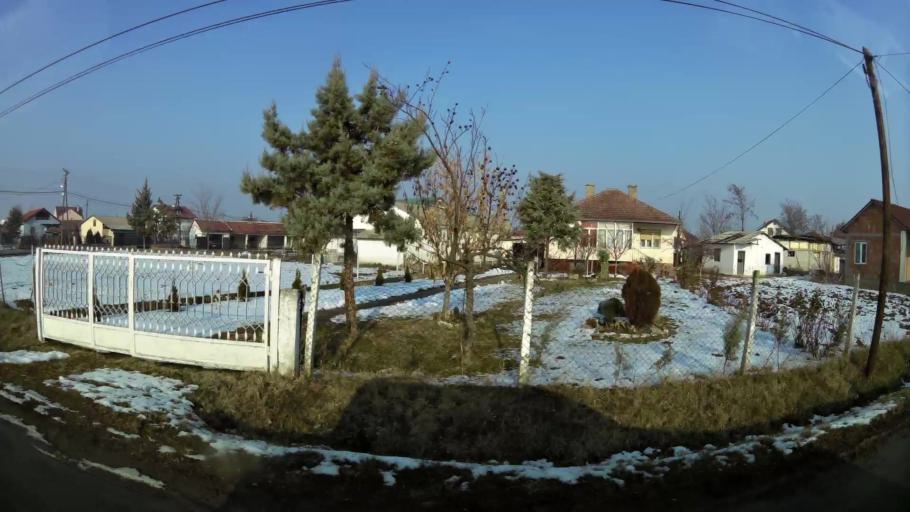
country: MK
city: Kadino
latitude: 41.9543
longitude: 21.6011
